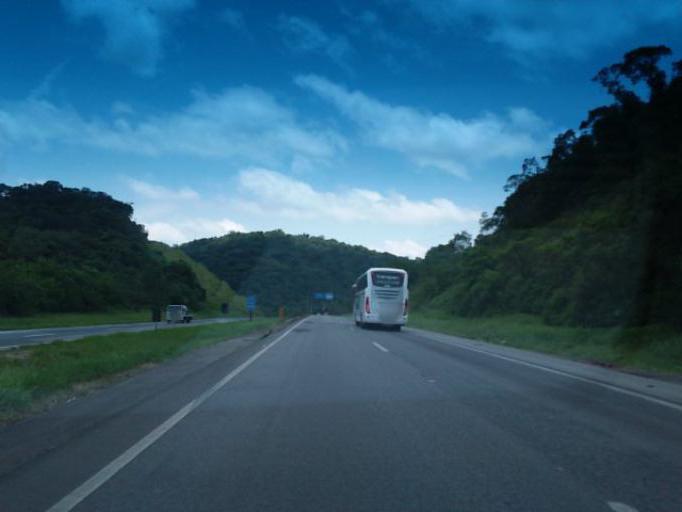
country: BR
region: Sao Paulo
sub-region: Juquia
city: Juquia
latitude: -24.3785
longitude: -47.7116
